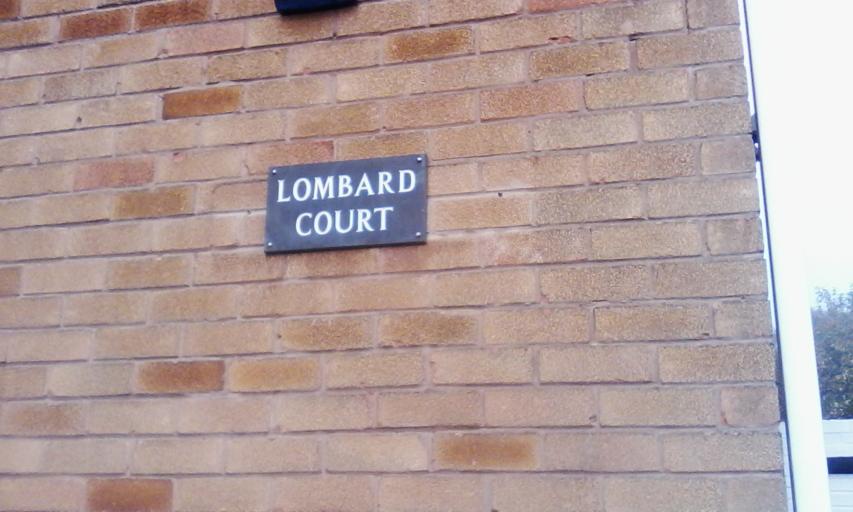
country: GB
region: England
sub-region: Nottinghamshire
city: Arnold
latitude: 52.9792
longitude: -1.1240
